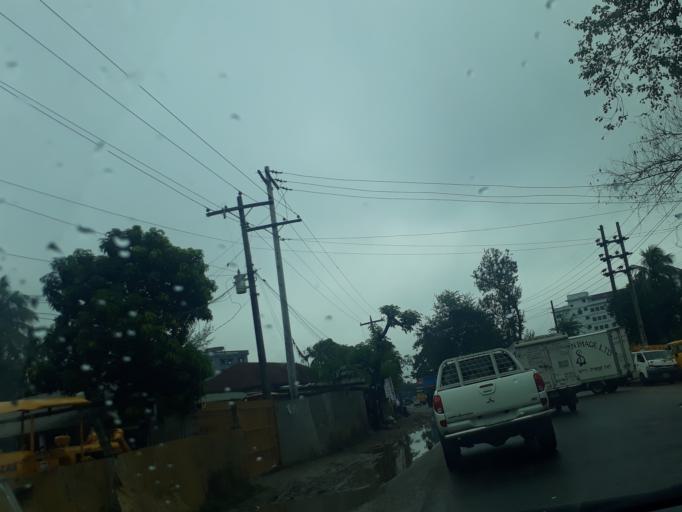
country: BD
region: Dhaka
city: Tungi
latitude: 23.9040
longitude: 90.3248
